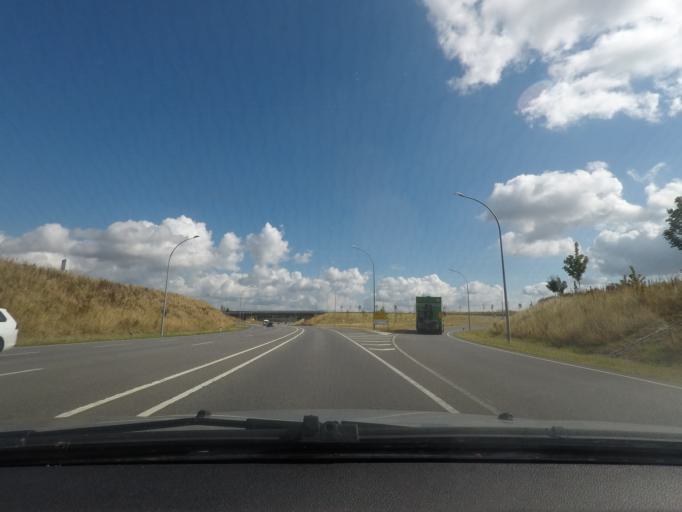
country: LU
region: Grevenmacher
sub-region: Canton de Grevenmacher
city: Junglinster
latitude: 49.7159
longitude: 6.2694
